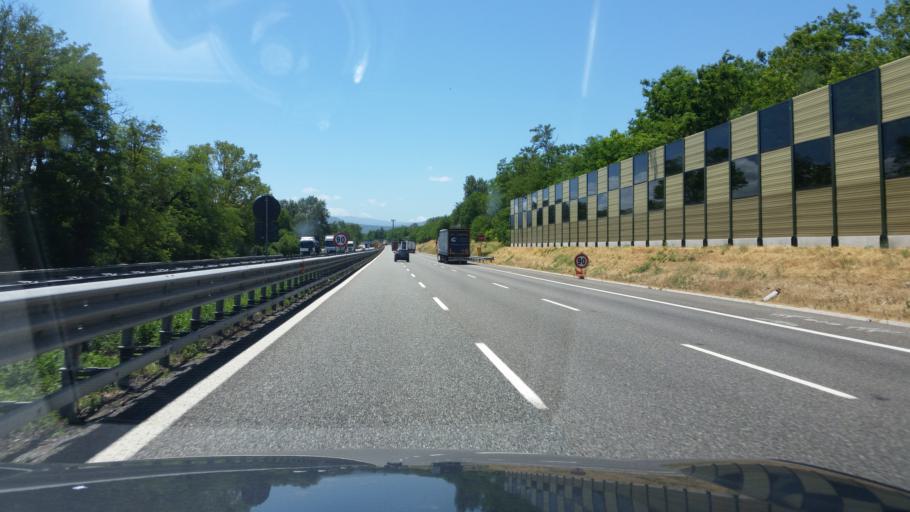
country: IT
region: Piedmont
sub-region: Provincia di Alessandria
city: Silvano d'Orba
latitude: 44.6838
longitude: 8.6616
